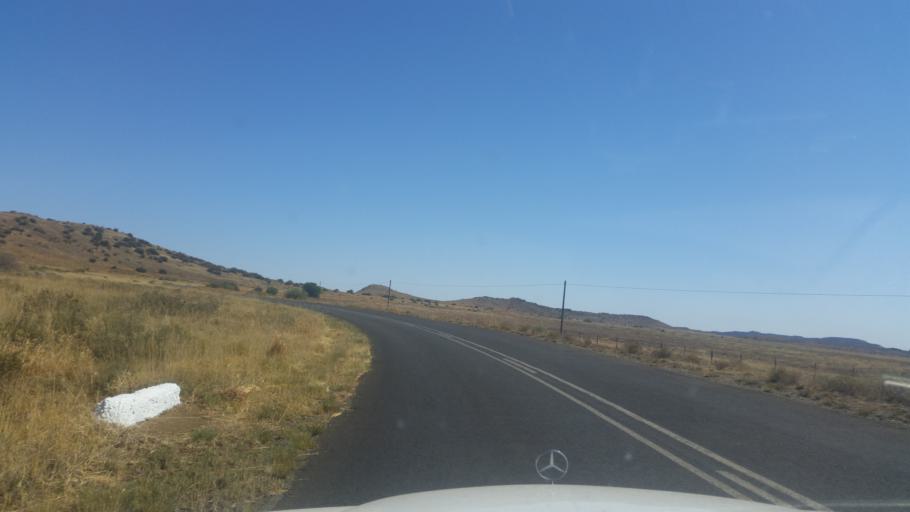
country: ZA
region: Eastern Cape
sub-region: Joe Gqabi District Municipality
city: Burgersdorp
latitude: -30.7417
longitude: 25.7571
